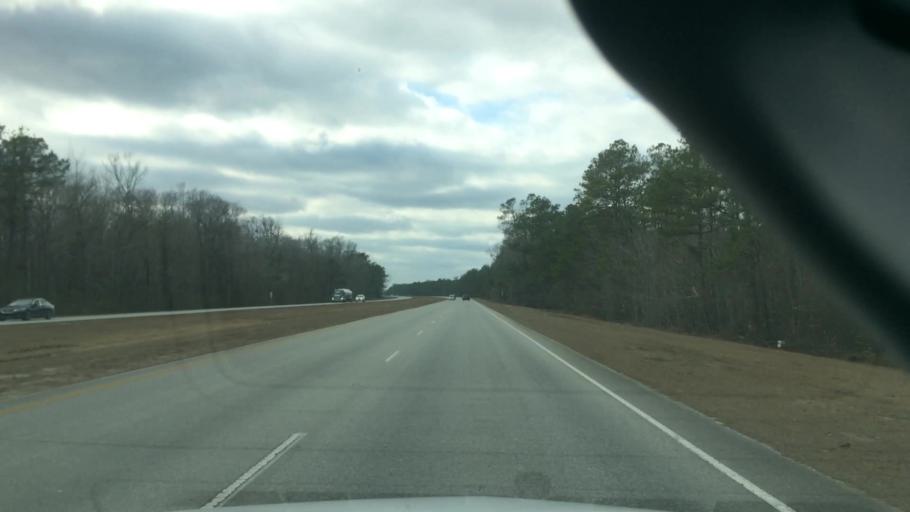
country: US
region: North Carolina
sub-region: Brunswick County
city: Bolivia
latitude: 34.0765
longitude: -78.1521
